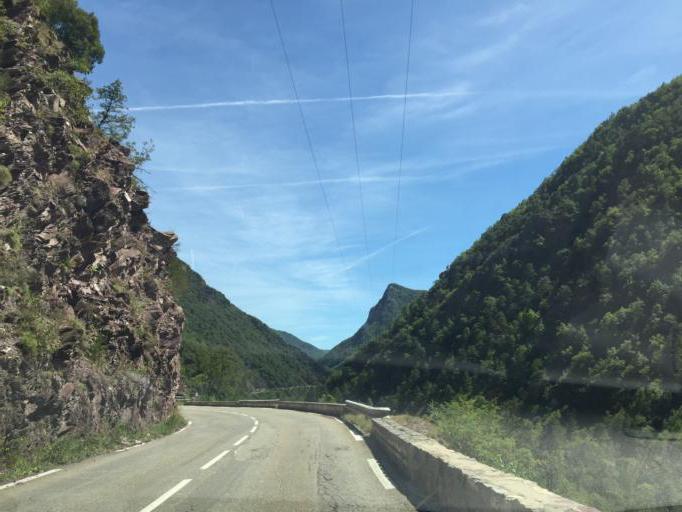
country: FR
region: Provence-Alpes-Cote d'Azur
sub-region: Departement des Alpes-Maritimes
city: Saint-Martin-Vesubie
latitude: 44.0702
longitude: 7.1104
